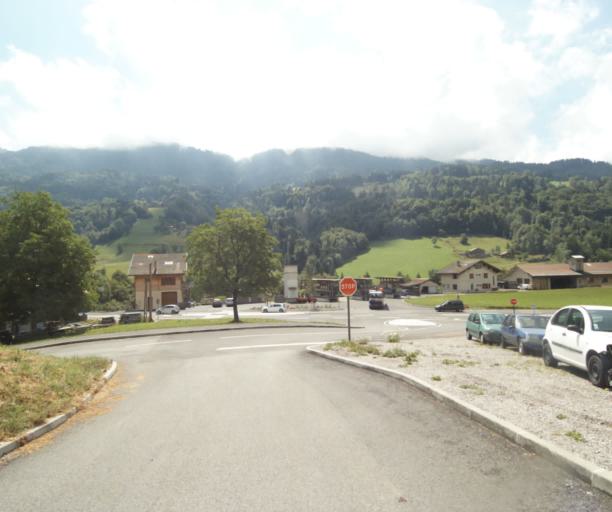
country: FR
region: Rhone-Alpes
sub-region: Departement de la Haute-Savoie
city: Thones
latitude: 45.9045
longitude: 6.3583
